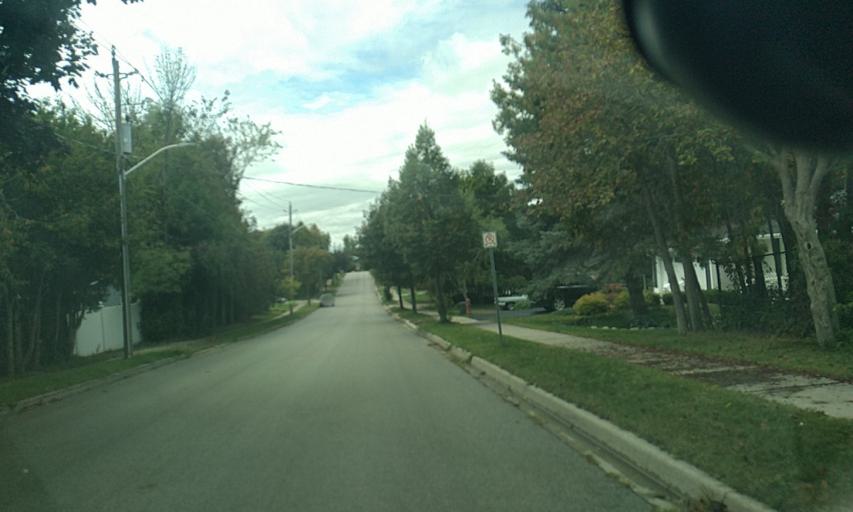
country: CA
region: Ontario
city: Newmarket
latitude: 44.0694
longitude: -79.4352
